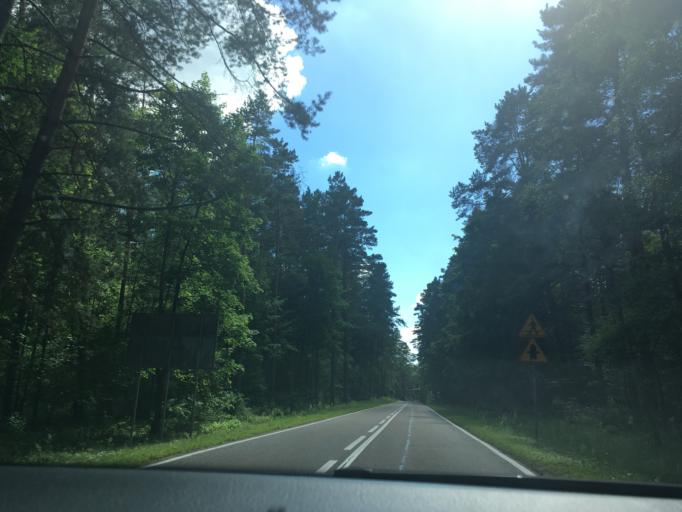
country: PL
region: Podlasie
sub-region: Powiat augustowski
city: Augustow
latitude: 53.8706
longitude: 23.0965
